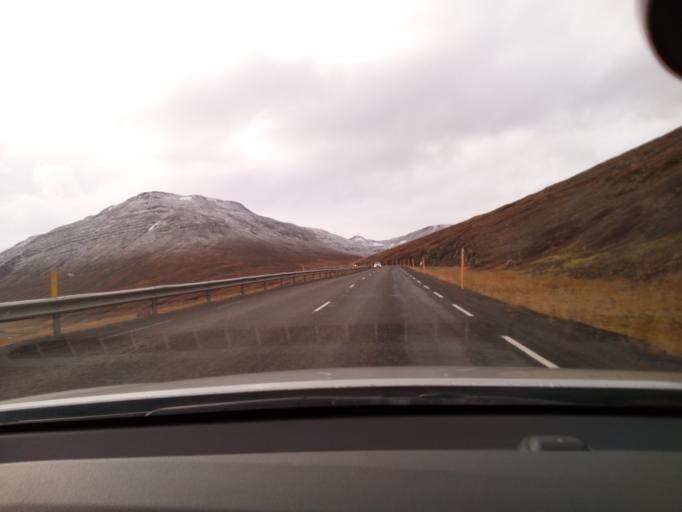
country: IS
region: Northeast
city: Dalvik
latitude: 65.4802
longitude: -18.6570
